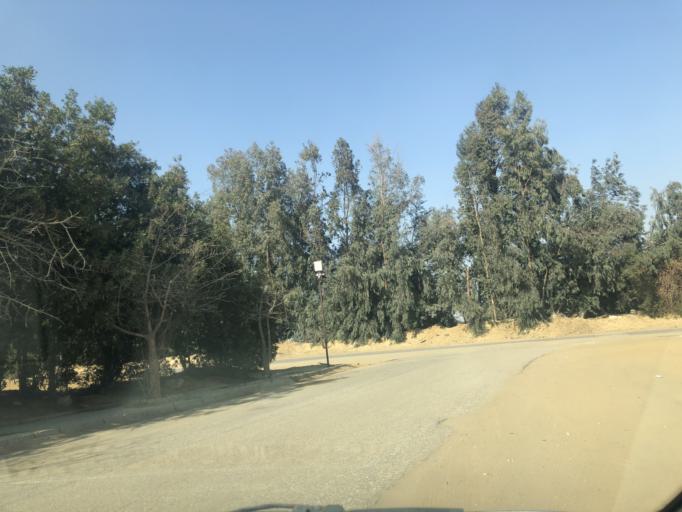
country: EG
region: Al Jizah
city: Madinat Sittah Uktubar
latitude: 29.9582
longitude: 31.0075
